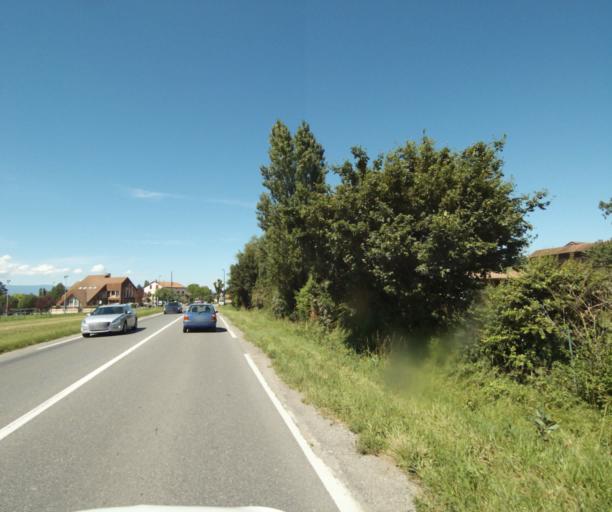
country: FR
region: Rhone-Alpes
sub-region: Departement de la Haute-Savoie
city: Loisin
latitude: 46.2869
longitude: 6.3094
